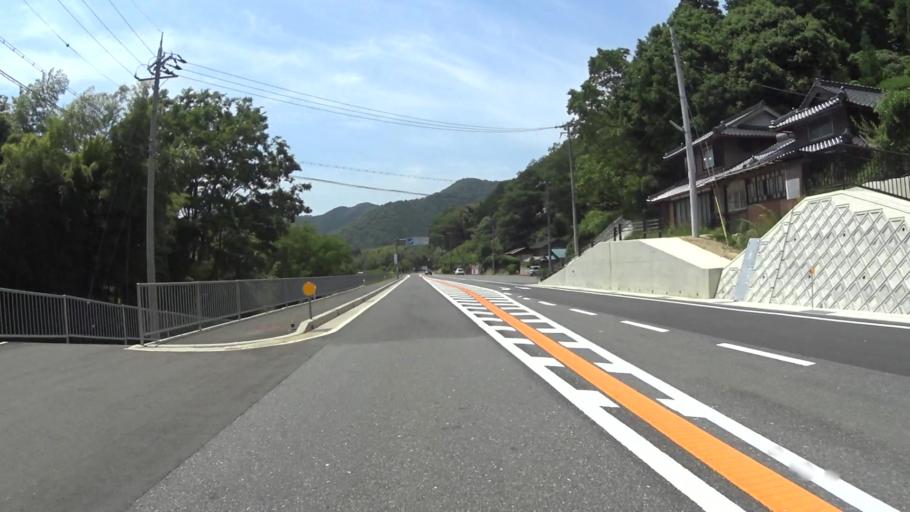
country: JP
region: Kyoto
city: Ayabe
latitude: 35.2008
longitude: 135.2512
